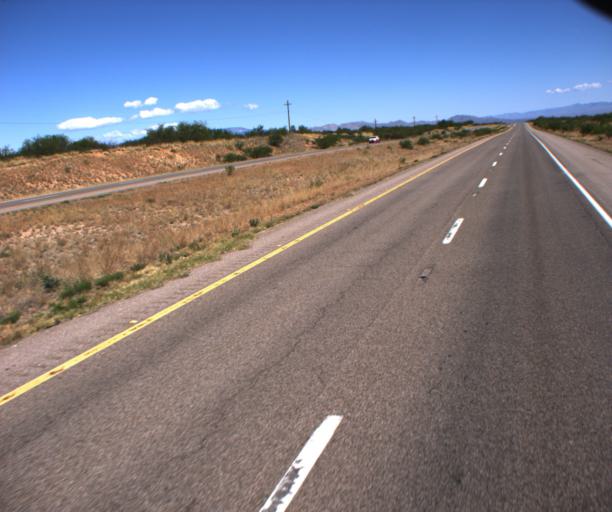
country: US
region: Arizona
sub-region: Cochise County
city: Whetstone
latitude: 31.8763
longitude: -110.3410
